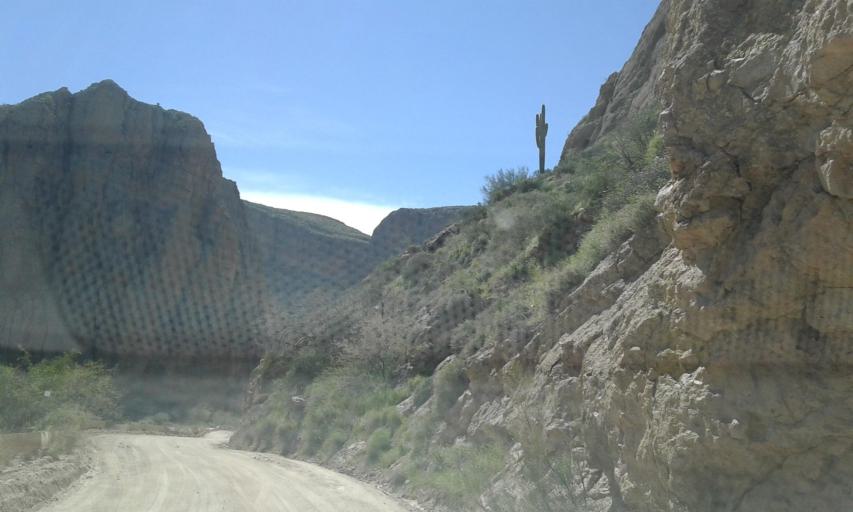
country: US
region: Arizona
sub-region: Pinal County
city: Gold Camp
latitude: 33.5316
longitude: -111.3088
